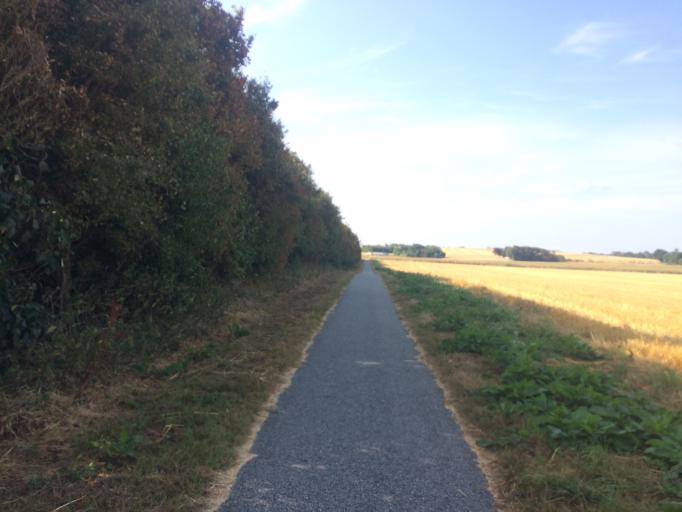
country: DK
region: Central Jutland
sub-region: Holstebro Kommune
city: Vinderup
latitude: 56.6071
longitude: 8.7719
